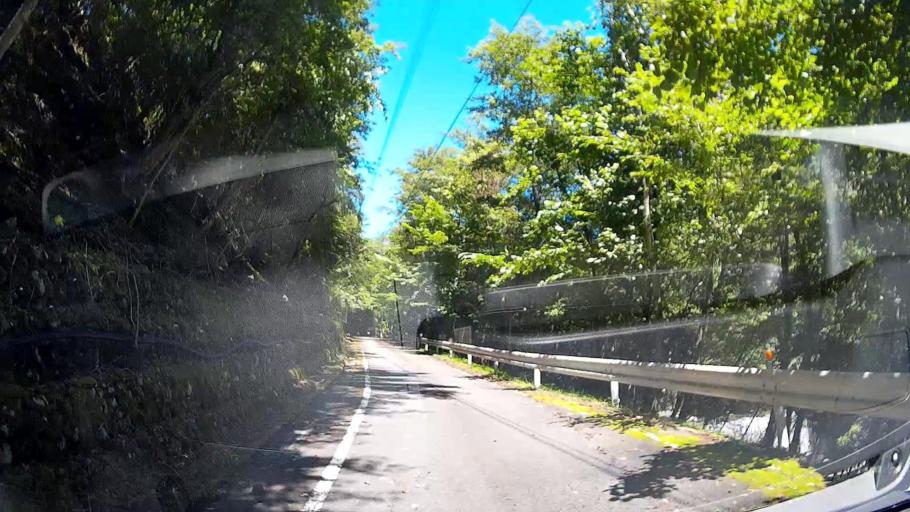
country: JP
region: Shizuoka
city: Fujinomiya
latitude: 35.2908
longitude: 138.3194
